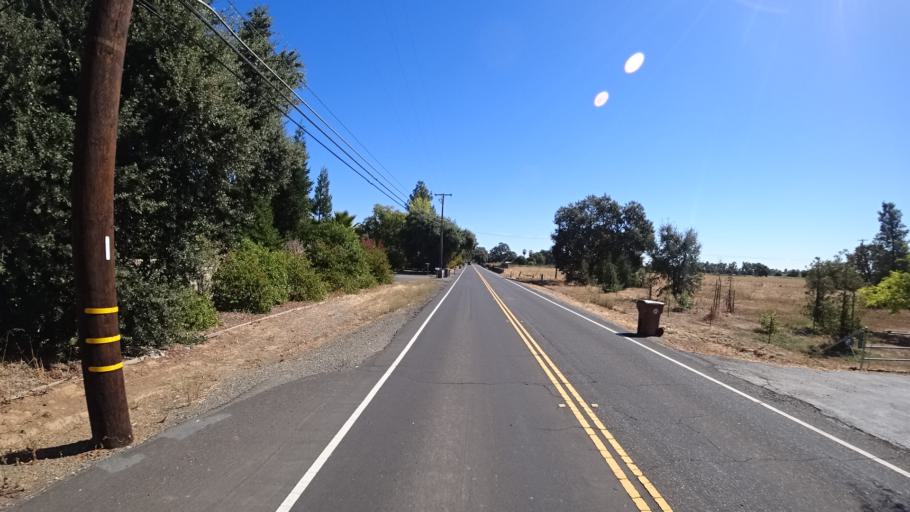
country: US
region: California
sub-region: Sacramento County
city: Elk Grove
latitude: 38.4237
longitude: -121.3305
